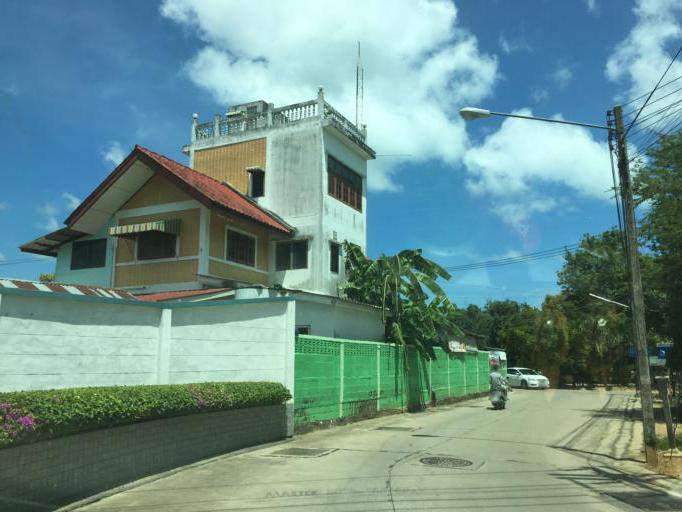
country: TH
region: Chon Buri
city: Sattahip
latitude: 12.7635
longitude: 100.8990
